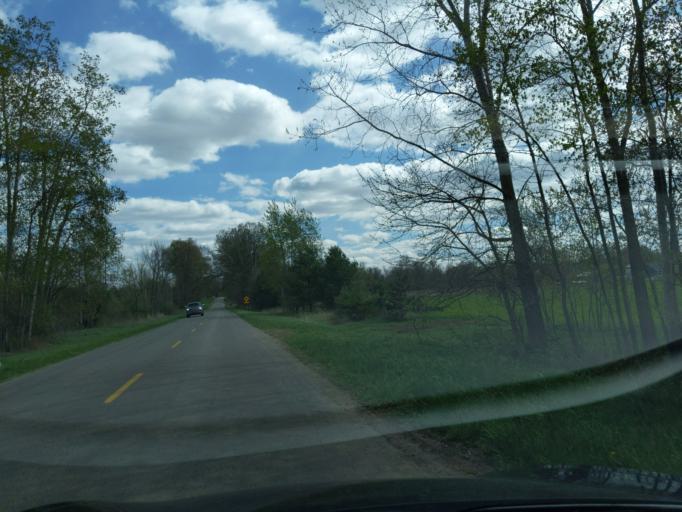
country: US
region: Michigan
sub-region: Eaton County
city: Eaton Rapids
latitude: 42.4968
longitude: -84.5463
